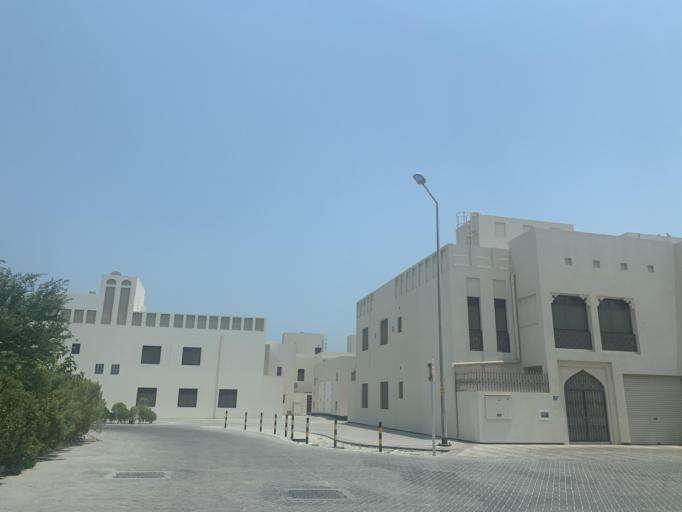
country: BH
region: Muharraq
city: Al Hadd
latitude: 26.2353
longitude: 50.6773
